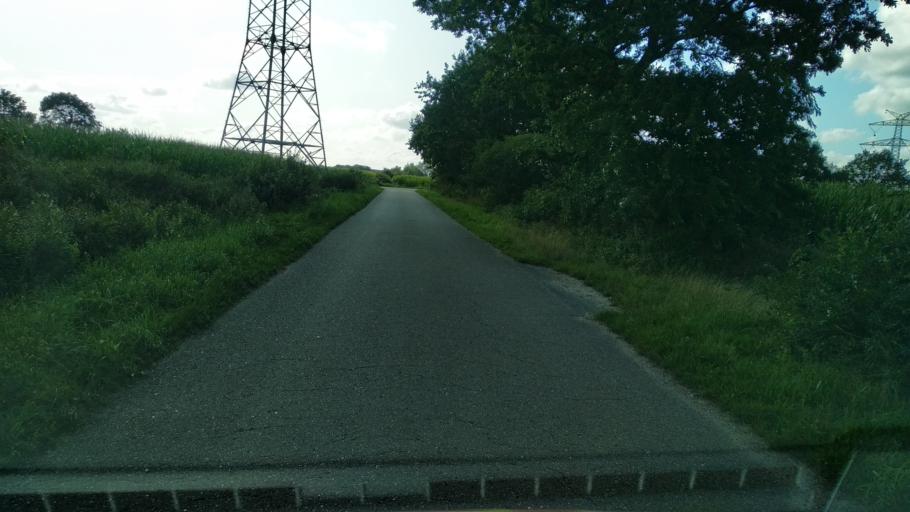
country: DE
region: Schleswig-Holstein
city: Gross Rheide
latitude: 54.4322
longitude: 9.4306
